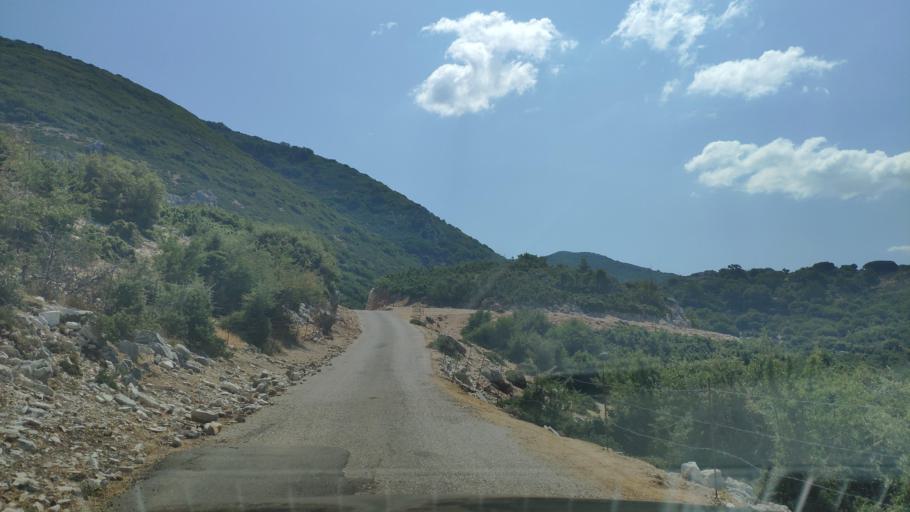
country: GR
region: West Greece
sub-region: Nomos Aitolias kai Akarnanias
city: Monastirakion
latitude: 38.8138
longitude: 20.9346
